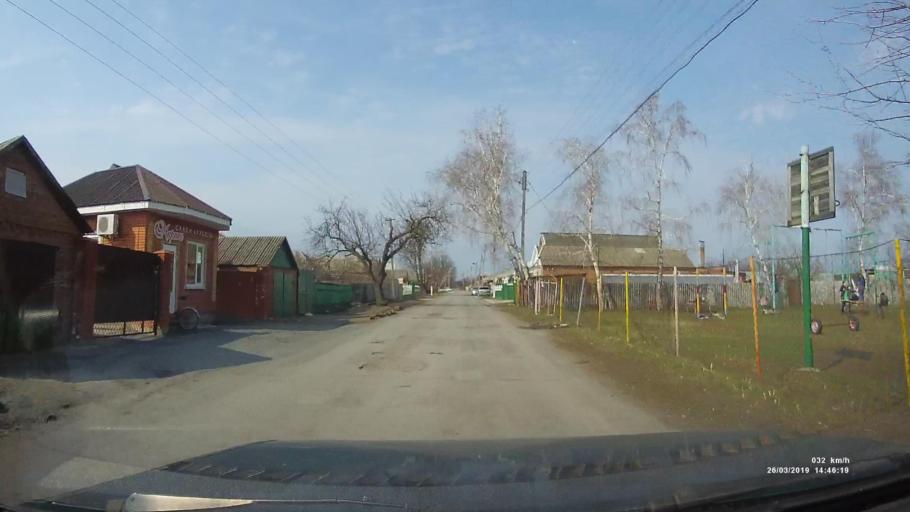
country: RU
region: Rostov
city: Novobessergenovka
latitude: 47.1859
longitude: 38.8606
